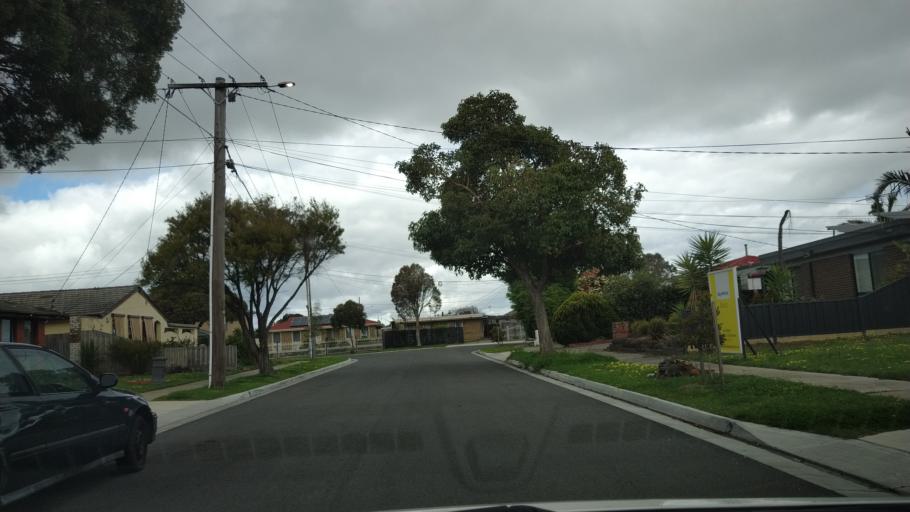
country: AU
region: Victoria
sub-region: Greater Dandenong
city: Keysborough
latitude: -37.9887
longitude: 145.1685
